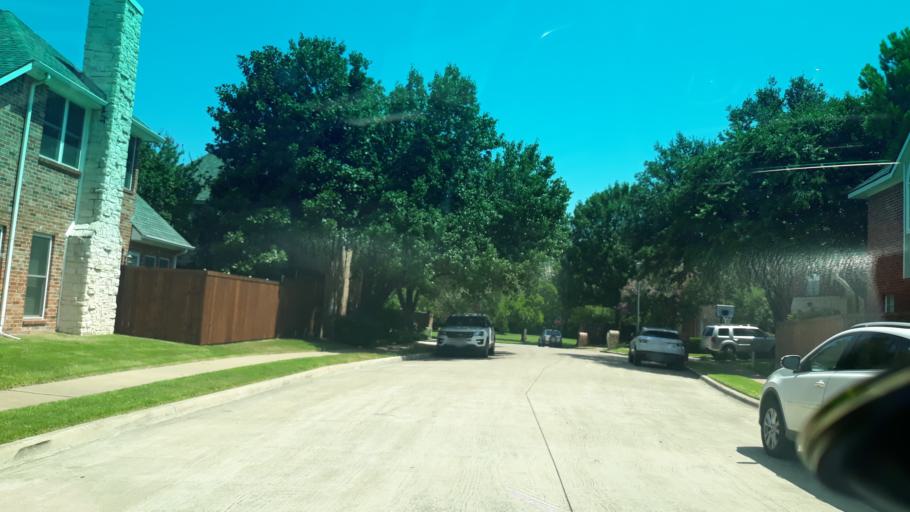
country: US
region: Texas
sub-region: Dallas County
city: Highland Park
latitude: 32.8157
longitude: -96.7316
